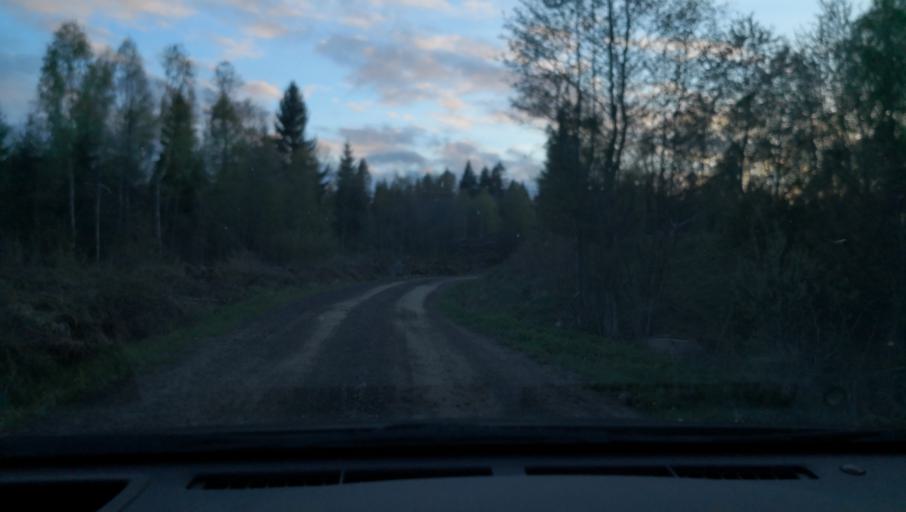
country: SE
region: OErebro
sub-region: Askersunds Kommun
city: Asbro
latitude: 58.9815
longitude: 14.9466
